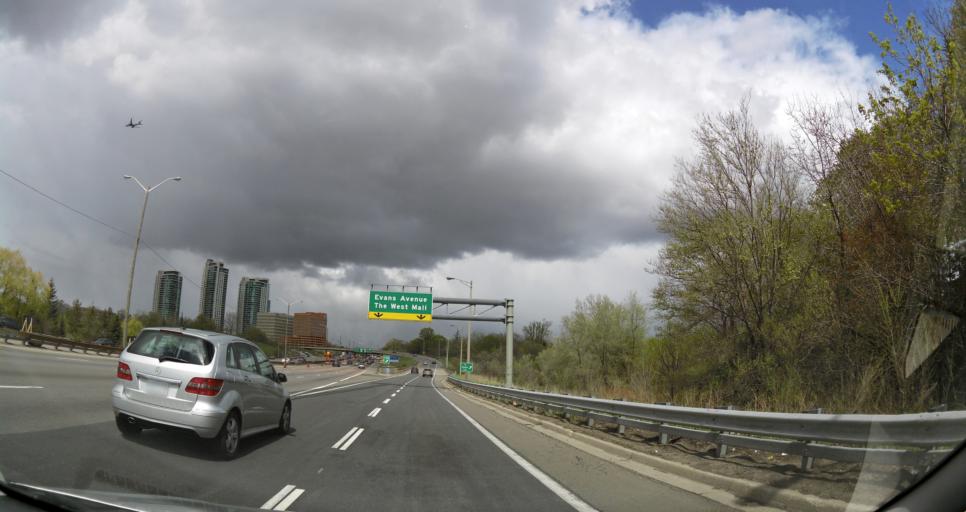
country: CA
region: Ontario
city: Etobicoke
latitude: 43.6036
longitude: -79.5609
